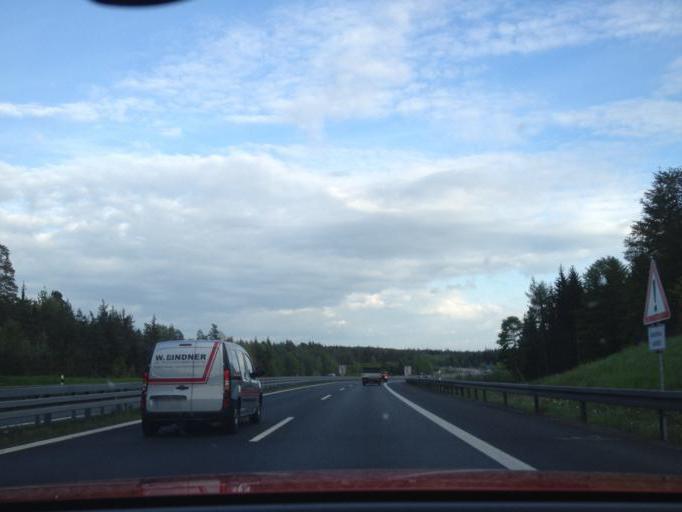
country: DE
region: Bavaria
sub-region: Upper Palatinate
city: Pechbrunn
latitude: 49.9605
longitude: 12.1894
